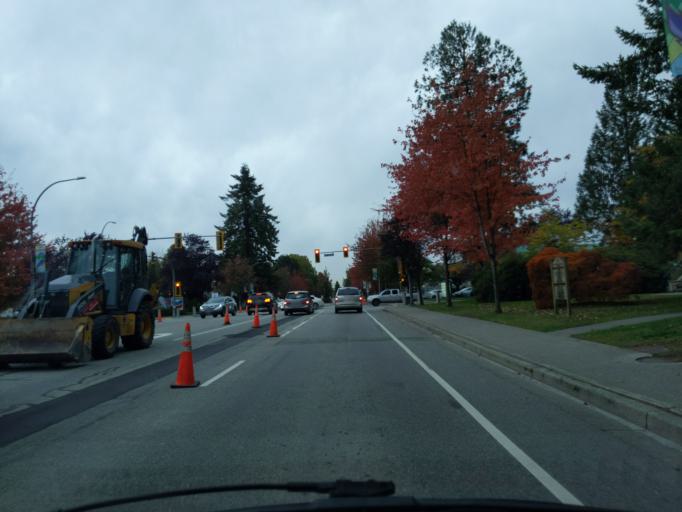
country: CA
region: British Columbia
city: Pitt Meadows
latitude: 49.2251
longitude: -122.6897
